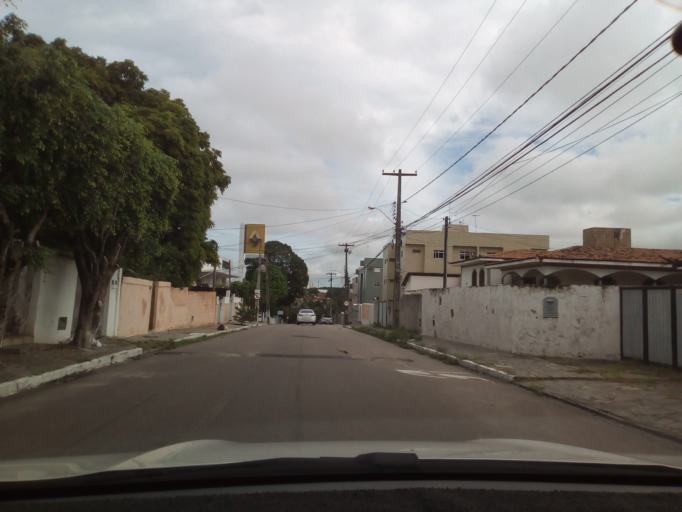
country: BR
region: Paraiba
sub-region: Joao Pessoa
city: Joao Pessoa
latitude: -7.1244
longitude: -34.8514
